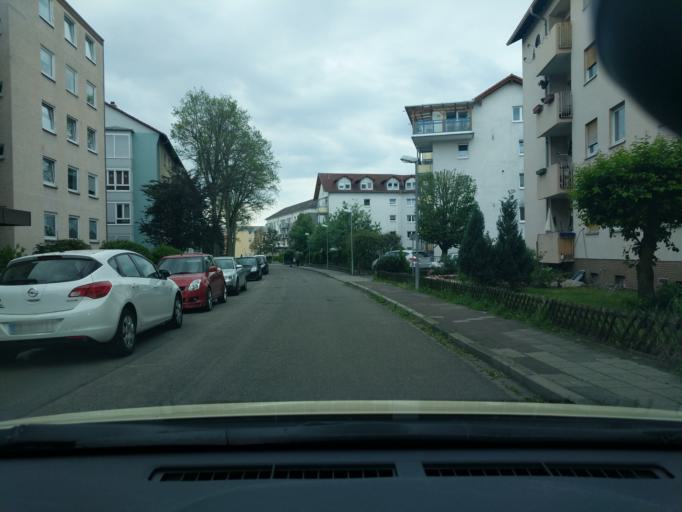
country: DE
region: Rheinland-Pfalz
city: Kaiserslautern
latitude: 49.4476
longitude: 7.7923
